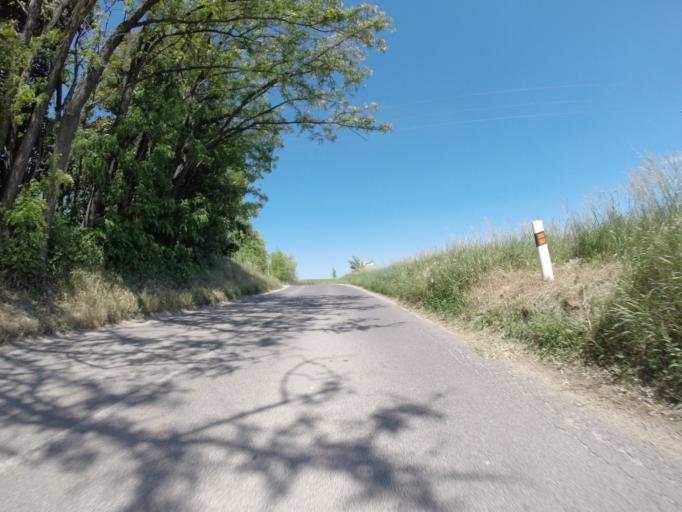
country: SK
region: Trnavsky
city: Hlohovec
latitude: 48.4686
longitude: 17.8553
